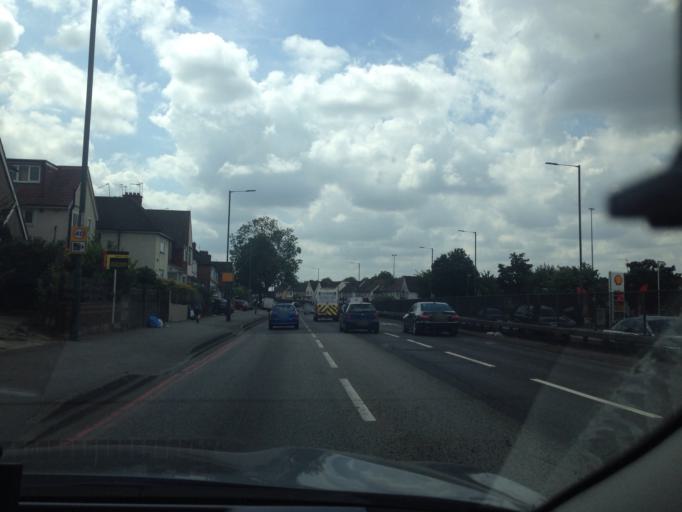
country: GB
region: England
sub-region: Greater London
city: Wembley
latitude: 51.5583
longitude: -0.2536
